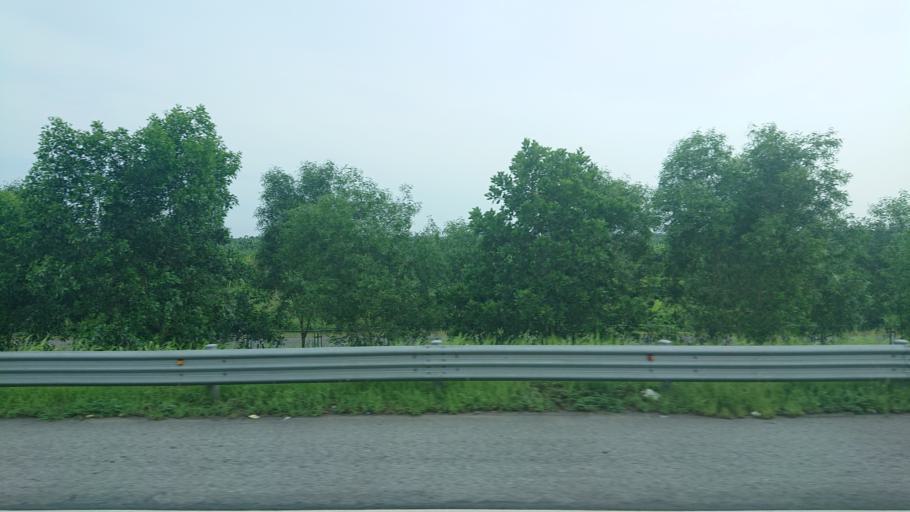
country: VN
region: Hai Duong
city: Tu Ky
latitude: 20.8283
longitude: 106.4550
